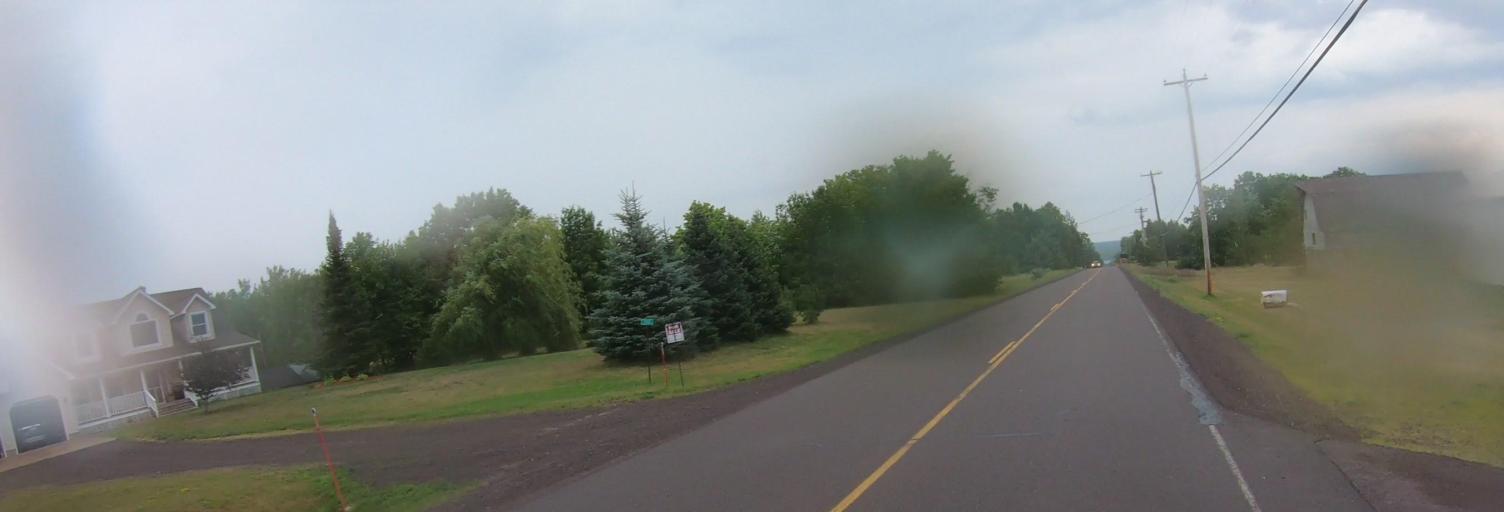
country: US
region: Michigan
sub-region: Houghton County
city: Houghton
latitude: 47.0253
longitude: -88.5461
